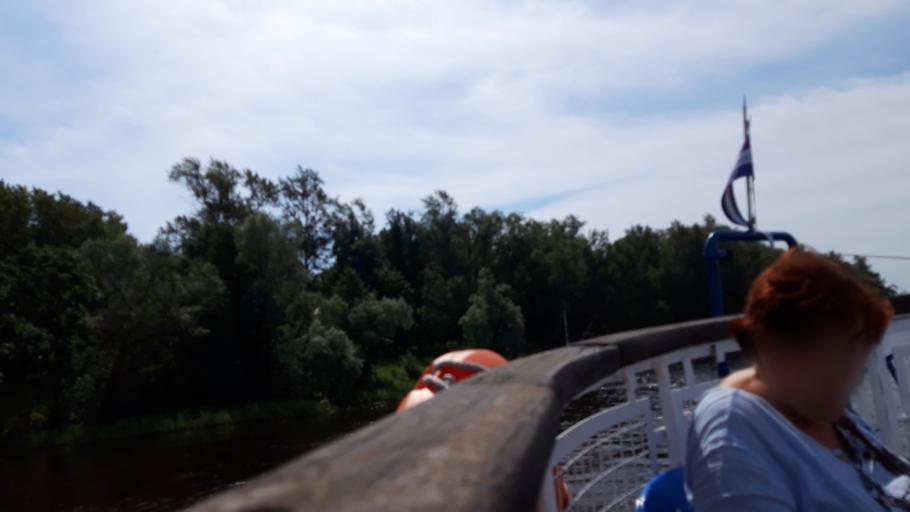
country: RU
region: Tverskaya
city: Konakovo
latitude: 56.6901
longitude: 36.6977
